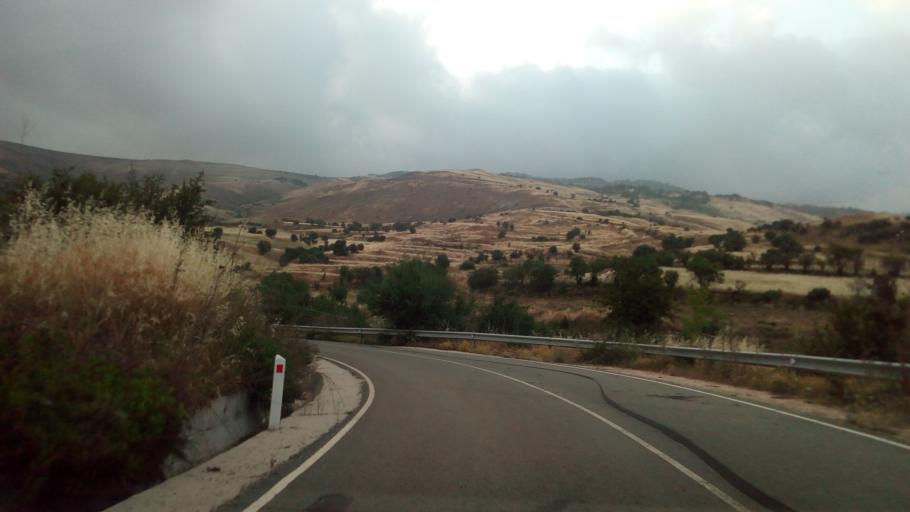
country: CY
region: Limassol
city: Pachna
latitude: 34.8668
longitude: 32.6386
